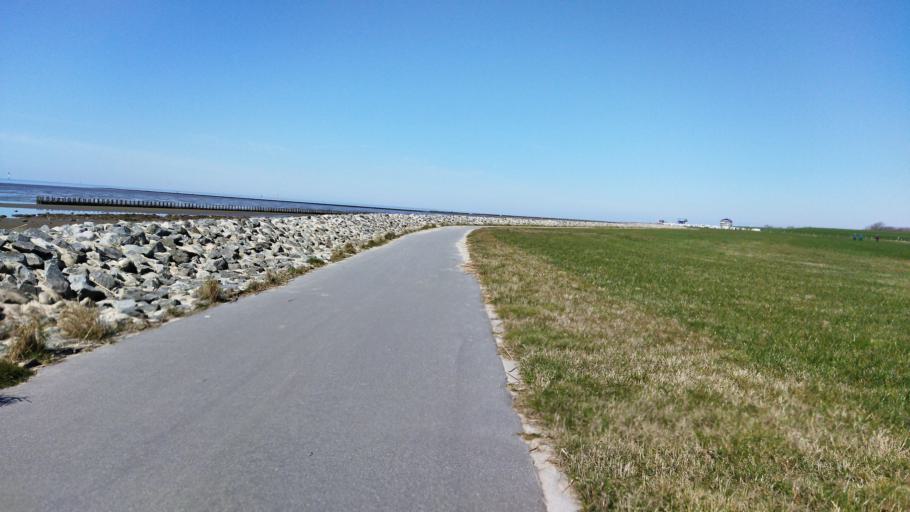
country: DE
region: Lower Saxony
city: Wremen
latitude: 53.6330
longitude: 8.5019
